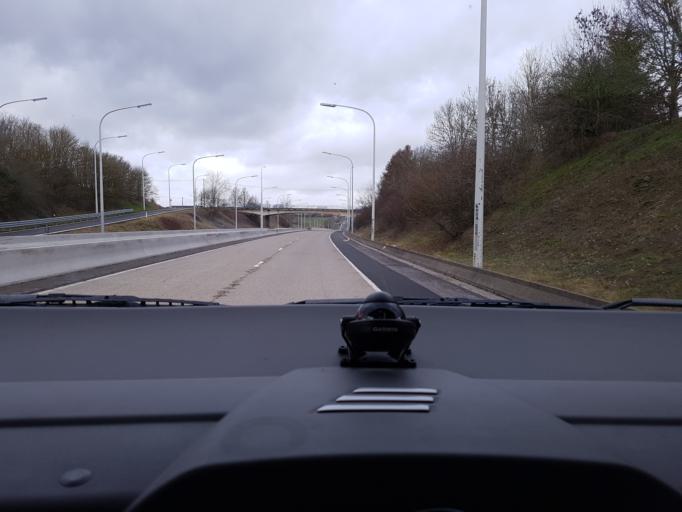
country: BE
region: Wallonia
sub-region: Province du Luxembourg
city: Marche-en-Famenne
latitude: 50.2671
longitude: 5.2471
